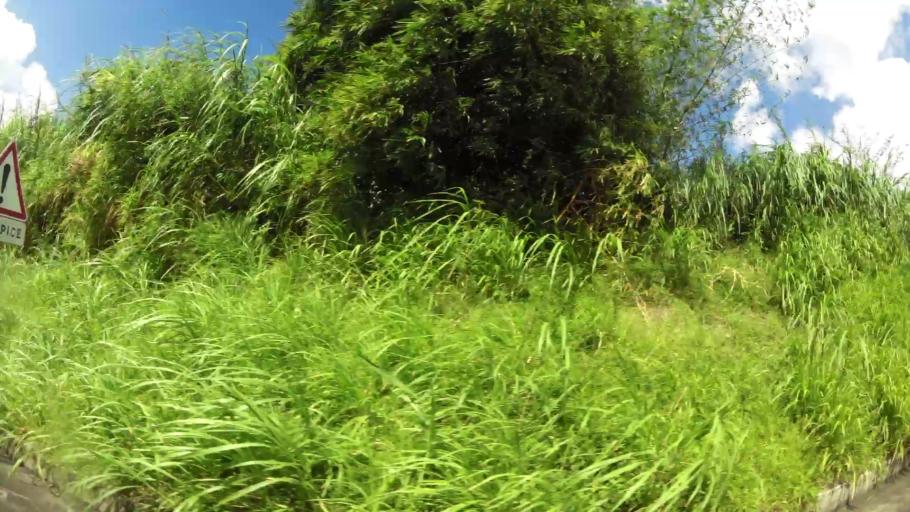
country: MQ
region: Martinique
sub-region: Martinique
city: Saint-Pierre
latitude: 14.7607
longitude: -61.1578
